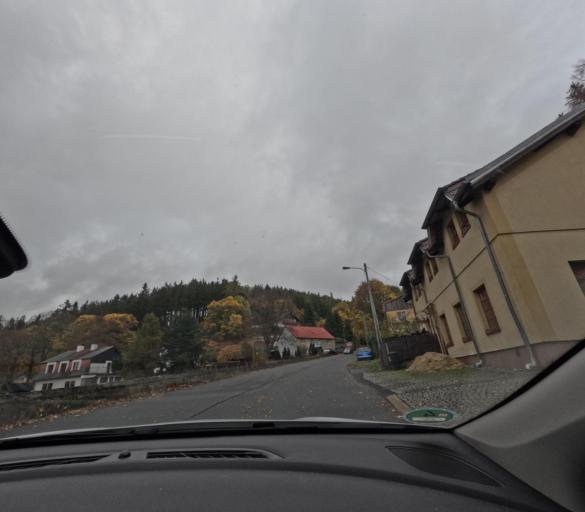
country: CZ
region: Karlovarsky
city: Dalovice
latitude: 50.2191
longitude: 12.9036
